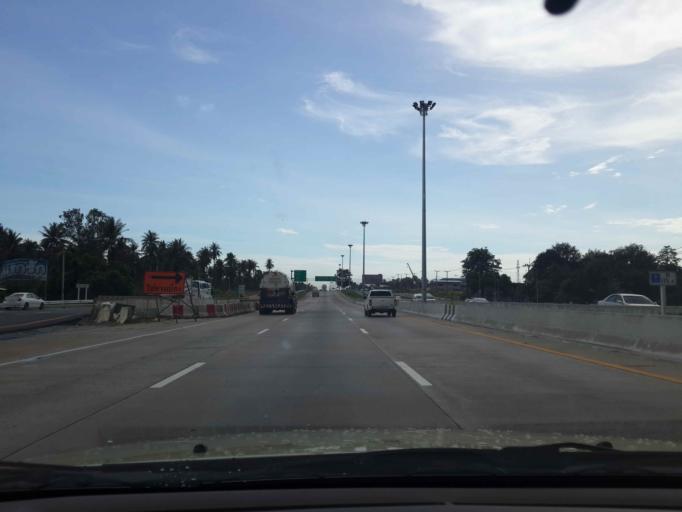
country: TH
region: Chon Buri
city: Bang Lamung
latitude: 12.9770
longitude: 100.9842
